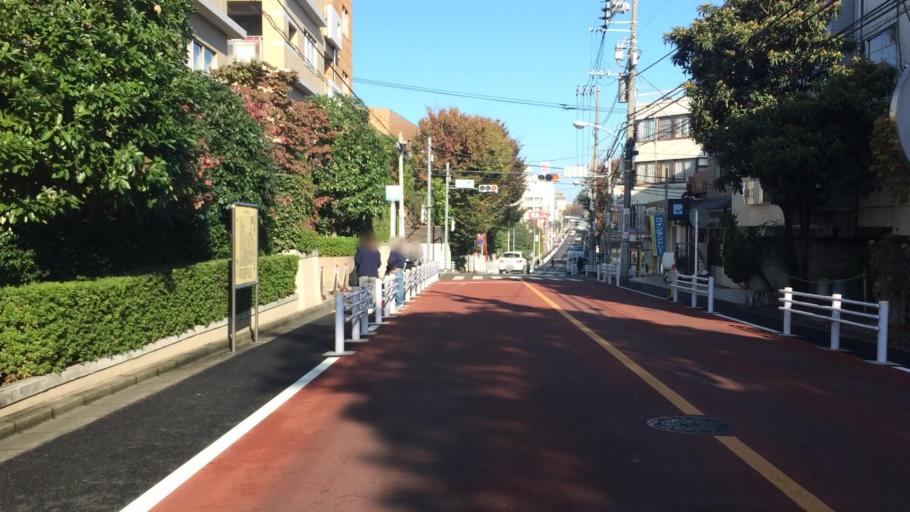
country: JP
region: Tokyo
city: Tokyo
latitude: 35.6201
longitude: 139.6673
